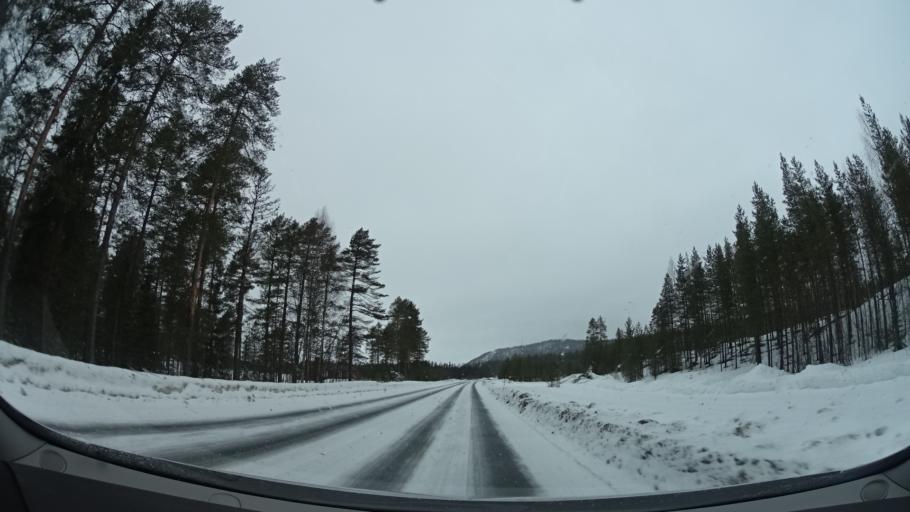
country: SE
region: Vaesterbotten
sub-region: Mala Kommun
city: Mala
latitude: 65.1592
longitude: 18.7851
